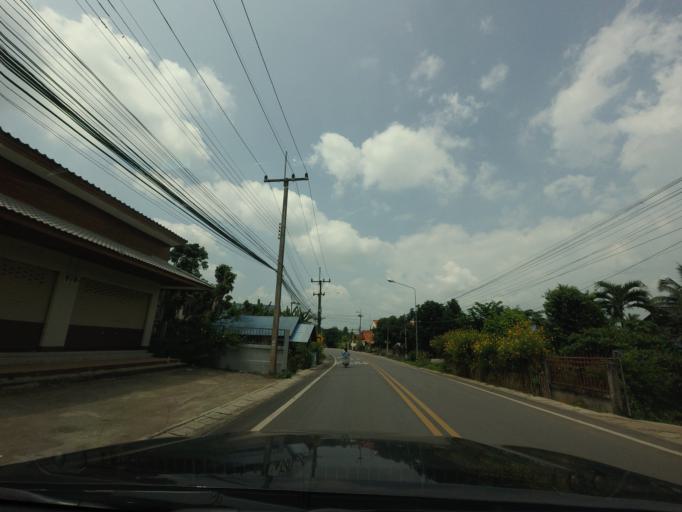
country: TH
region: Nan
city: Pua
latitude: 19.1560
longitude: 100.9320
